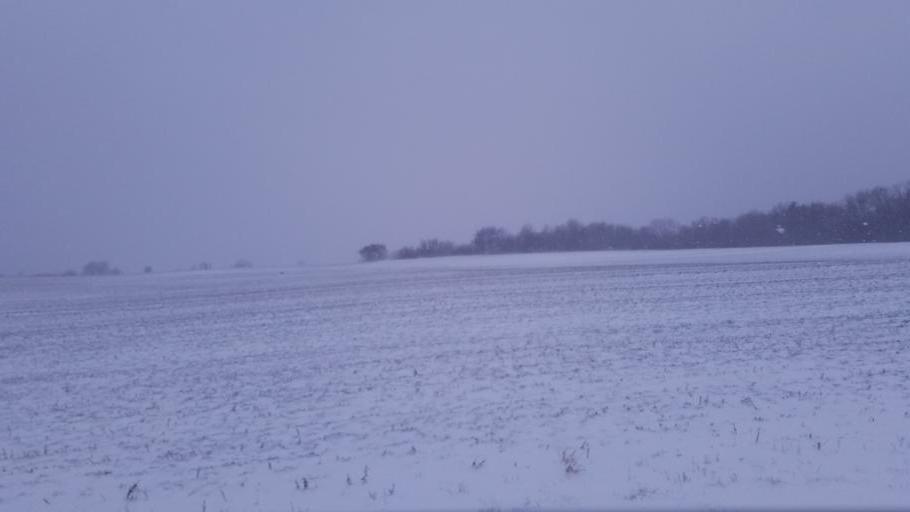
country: US
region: Ohio
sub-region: Knox County
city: Fredericktown
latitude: 40.4958
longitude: -82.6118
